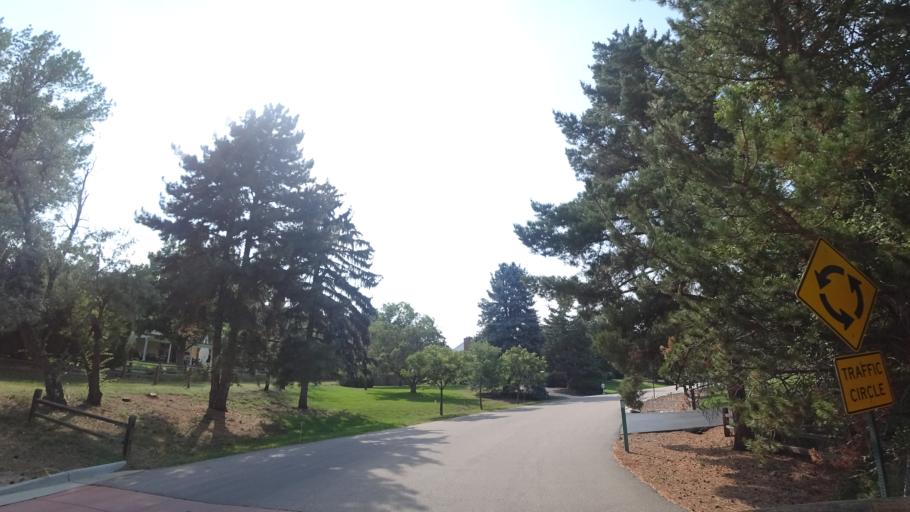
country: US
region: Colorado
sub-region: Arapahoe County
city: Greenwood Village
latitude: 39.6135
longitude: -104.9607
